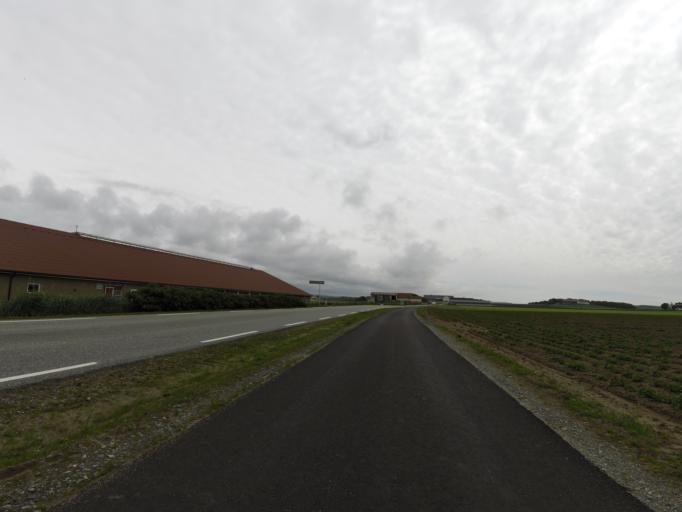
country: NO
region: Rogaland
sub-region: Ha
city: Naerbo
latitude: 58.6859
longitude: 5.5621
